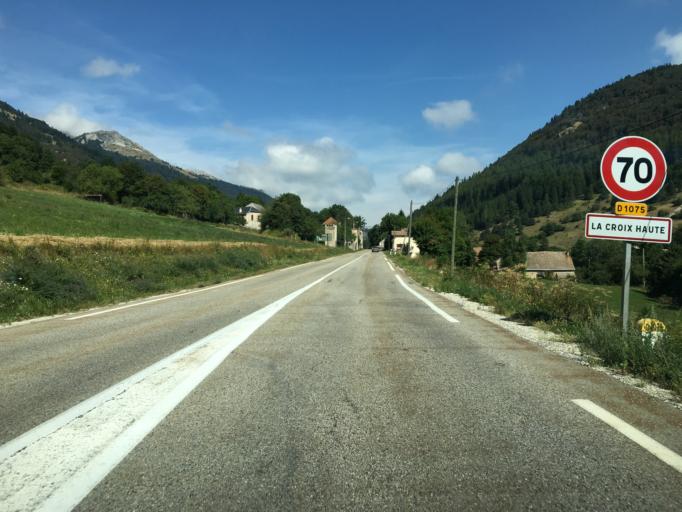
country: FR
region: Rhone-Alpes
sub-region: Departement de l'Isere
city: Mens
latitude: 44.6985
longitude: 5.6827
